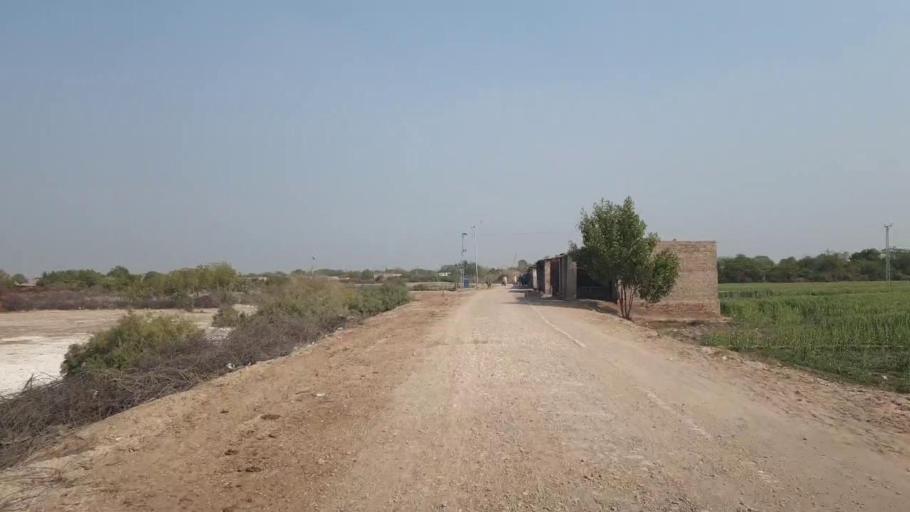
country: PK
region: Sindh
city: Mirwah Gorchani
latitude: 25.3512
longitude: 68.9489
